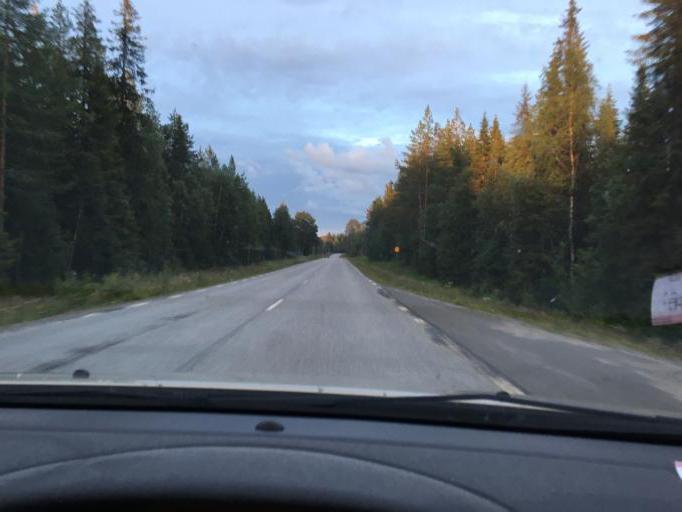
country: SE
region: Norrbotten
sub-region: Lulea Kommun
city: Ranea
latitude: 66.0474
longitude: 22.2775
